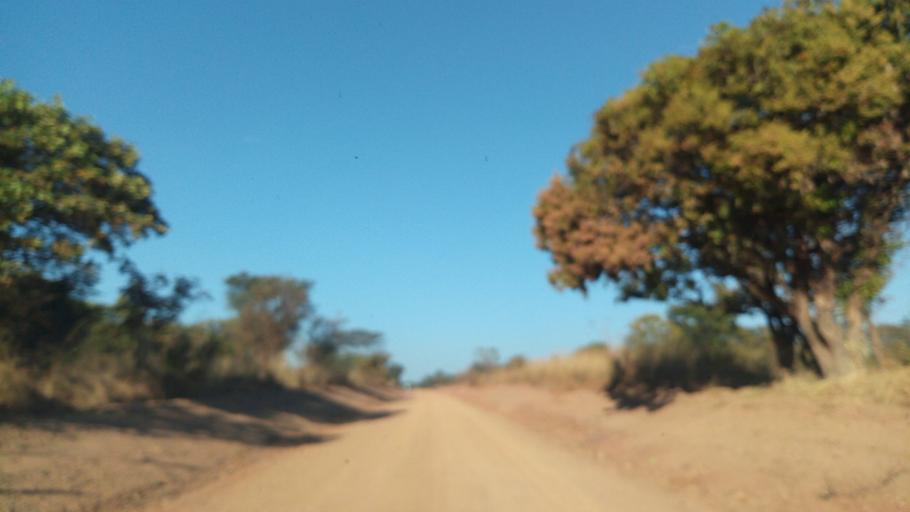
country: ZM
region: Luapula
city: Mwense
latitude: -10.4661
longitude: 28.5204
